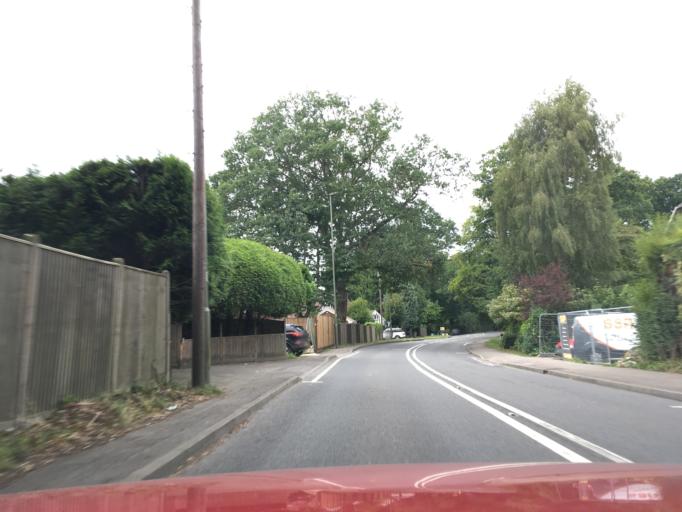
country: GB
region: England
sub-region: Surrey
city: Felbridge
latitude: 51.1409
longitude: -0.0505
